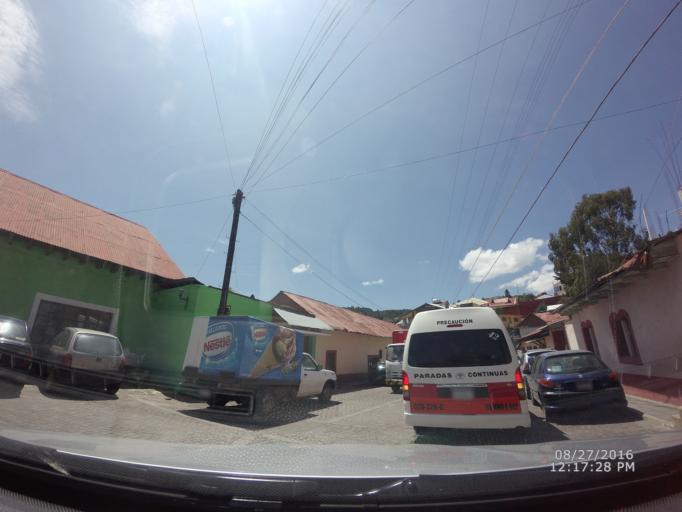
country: MX
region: Hidalgo
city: Mineral del Monte
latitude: 20.1389
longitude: -98.6713
